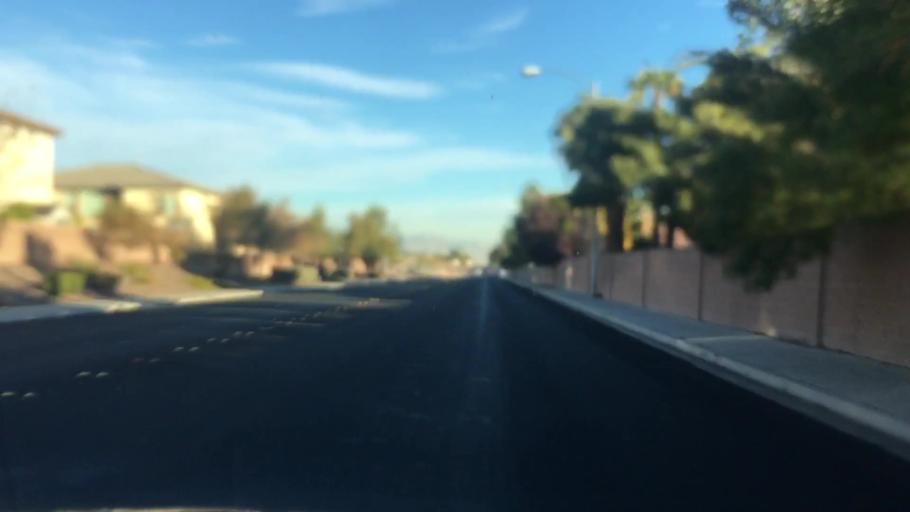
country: US
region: Nevada
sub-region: Clark County
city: Paradise
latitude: 36.0476
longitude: -115.1498
